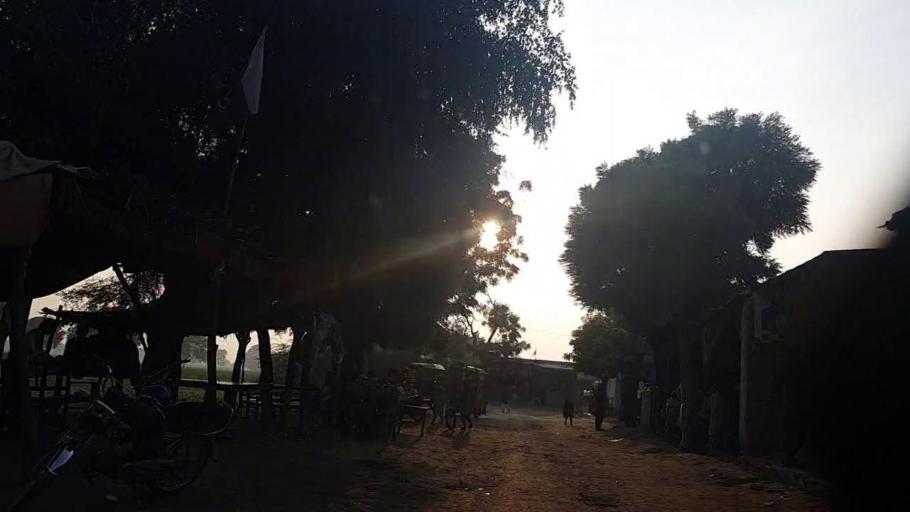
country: PK
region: Sindh
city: Sakrand
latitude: 26.1153
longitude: 68.2305
